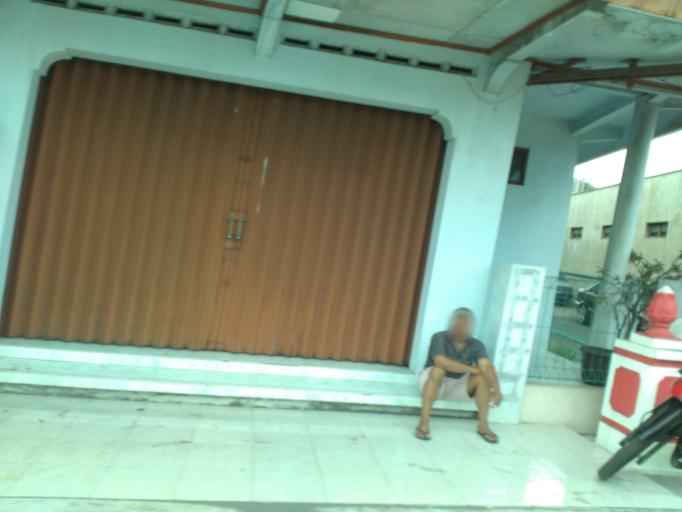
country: ID
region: Central Java
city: Trucuk
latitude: -7.6854
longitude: 110.6422
